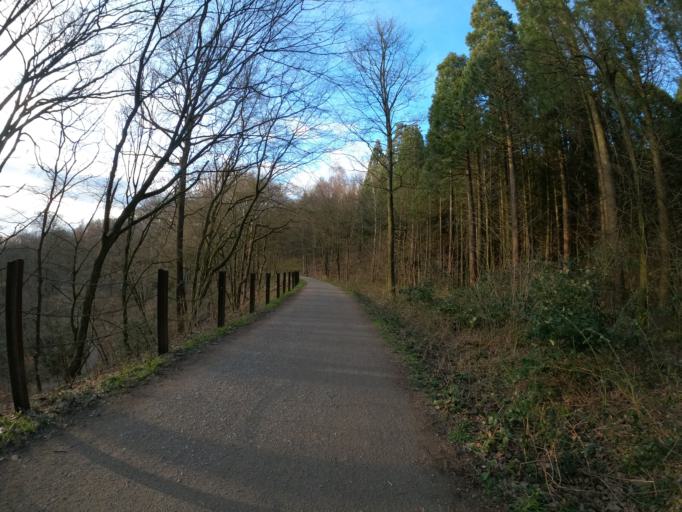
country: DE
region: North Rhine-Westphalia
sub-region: Regierungsbezirk Dusseldorf
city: Wuppertal
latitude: 51.2262
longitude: 7.1267
